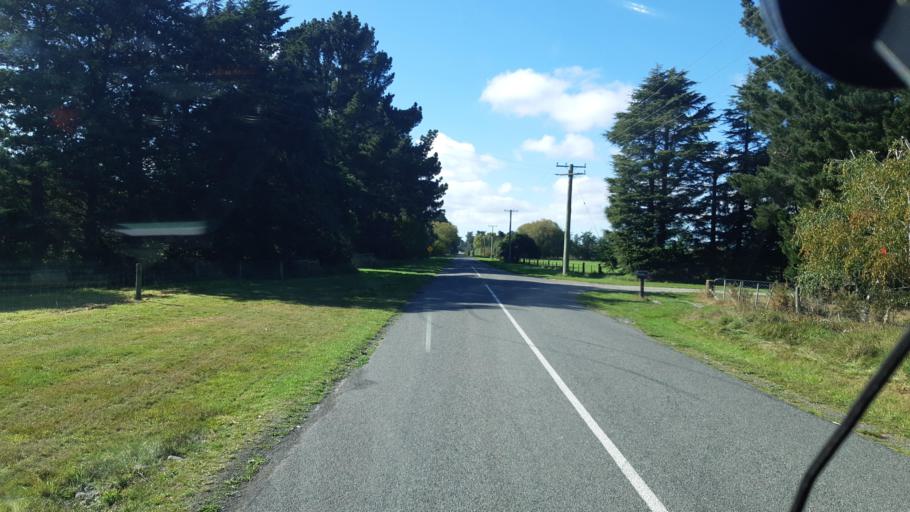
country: NZ
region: Canterbury
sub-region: Waimakariri District
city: Woodend
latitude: -43.2669
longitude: 172.5305
